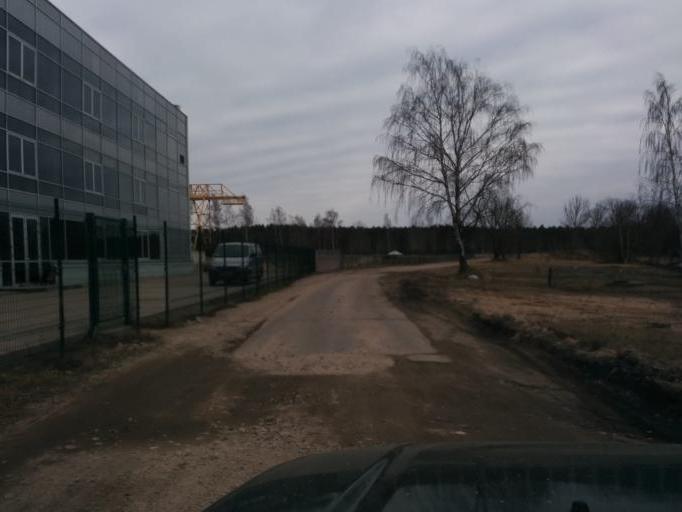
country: LV
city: Tireli
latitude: 56.9416
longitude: 23.6397
